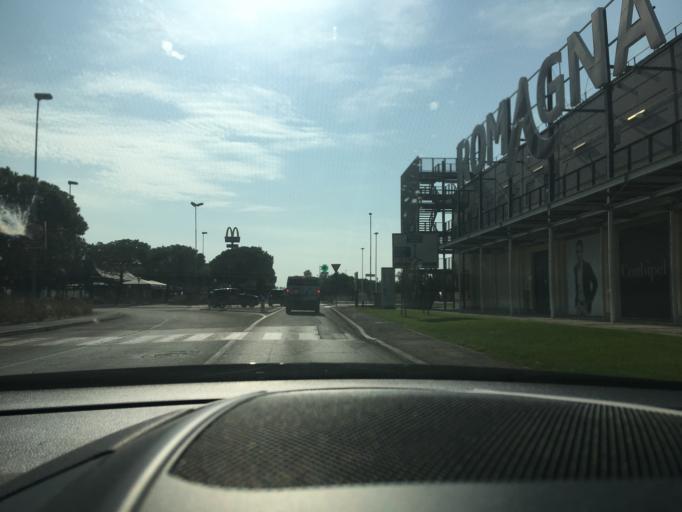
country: IT
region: Emilia-Romagna
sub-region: Forli-Cesena
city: Gatteo a Mare
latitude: 44.1571
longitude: 12.4315
